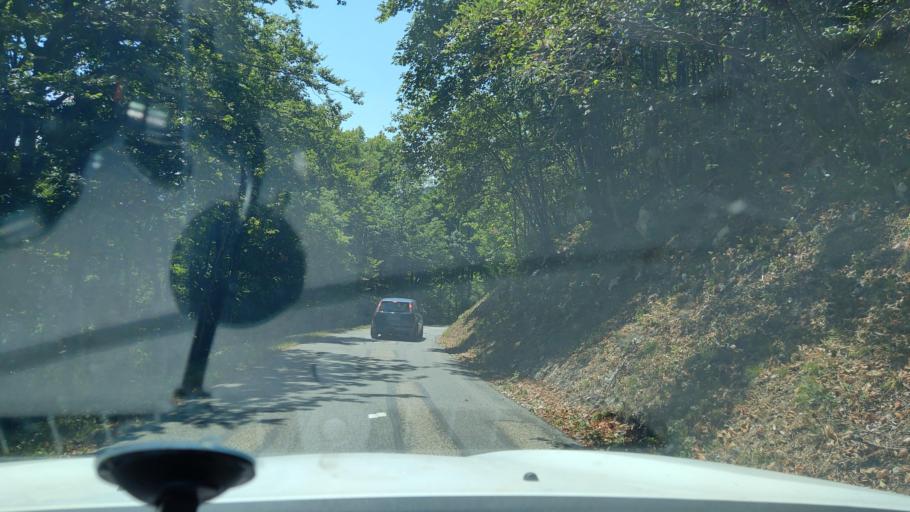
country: FR
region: Rhone-Alpes
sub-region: Departement de la Savoie
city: Le Bourget-du-Lac
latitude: 45.6595
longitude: 5.8362
